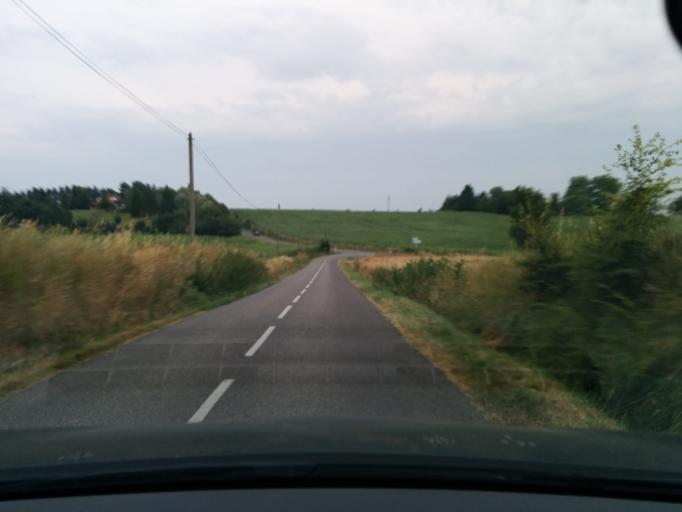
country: FR
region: Midi-Pyrenees
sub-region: Departement de la Haute-Garonne
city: Castanet-Tolosan
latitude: 43.5020
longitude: 1.4853
